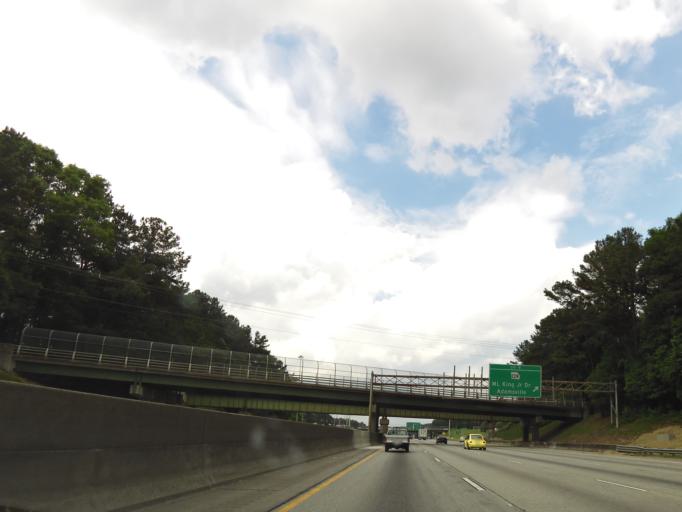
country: US
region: Georgia
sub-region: Fulton County
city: East Point
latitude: 33.7499
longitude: -84.4969
